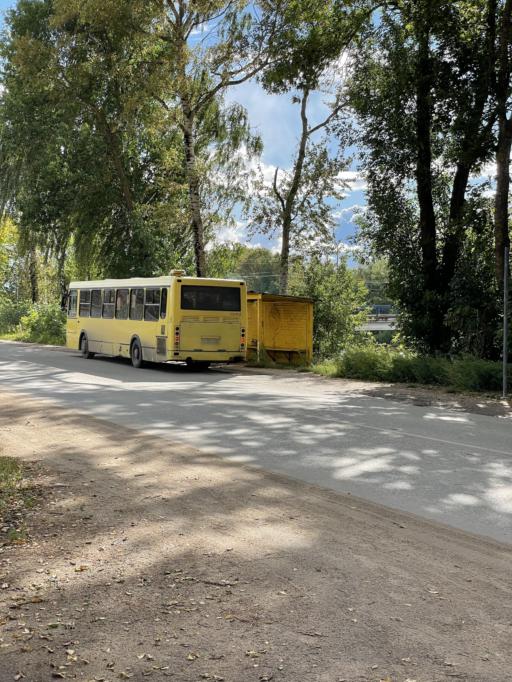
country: RU
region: Tverskaya
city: Vyshniy Volochek
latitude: 57.5752
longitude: 34.5552
